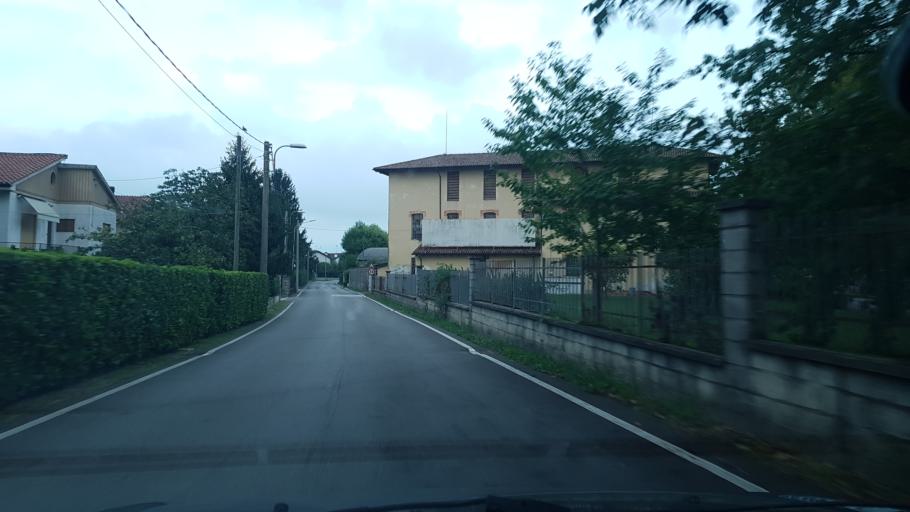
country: IT
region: Friuli Venezia Giulia
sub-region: Provincia di Gorizia
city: Romans d'Isonzo
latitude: 45.8941
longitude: 13.4306
